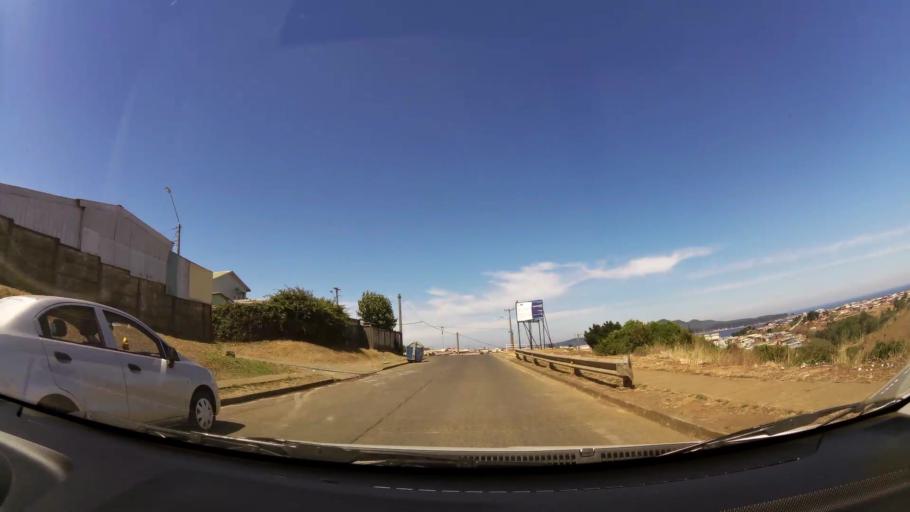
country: CL
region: Biobio
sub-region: Provincia de Concepcion
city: Talcahuano
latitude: -36.7161
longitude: -73.1411
